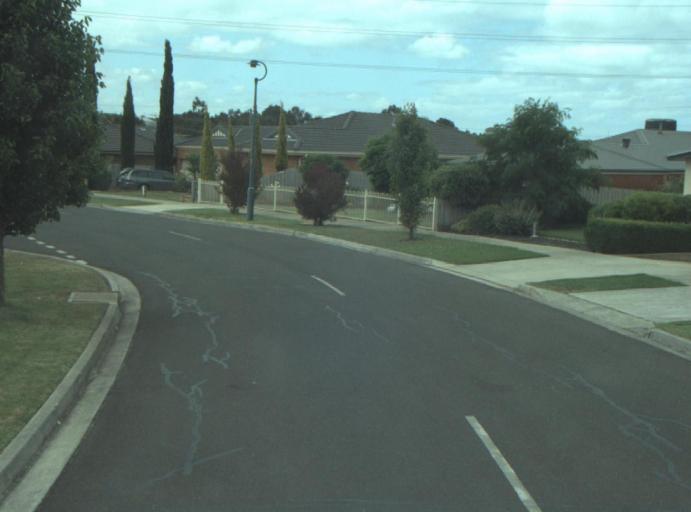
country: AU
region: Victoria
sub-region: Greater Geelong
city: Wandana Heights
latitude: -38.1948
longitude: 144.3138
